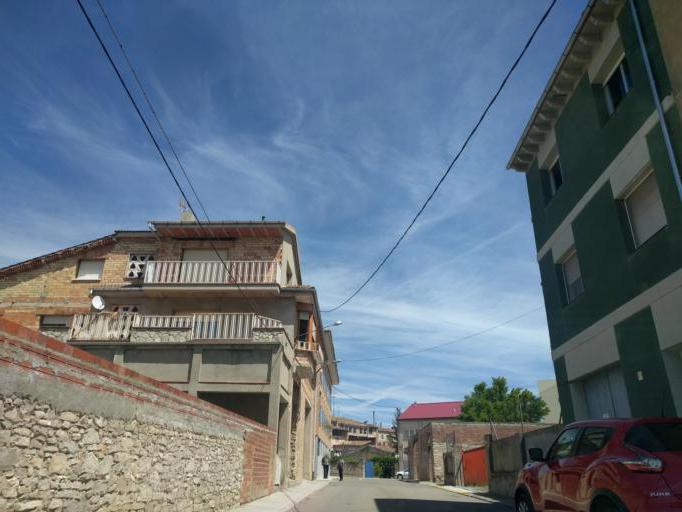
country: ES
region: Catalonia
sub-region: Provincia de Tarragona
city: Santa Coloma de Queralt
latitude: 41.5347
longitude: 1.3841
